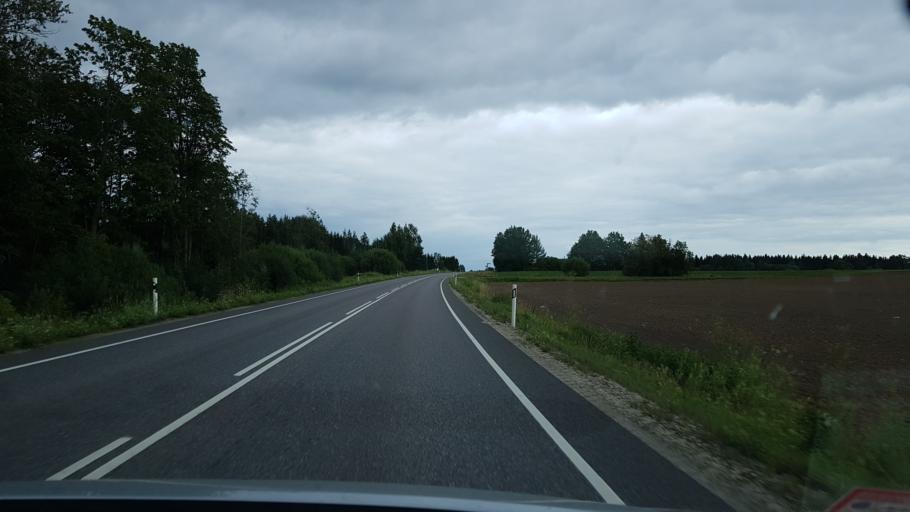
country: EE
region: Tartu
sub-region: Tartu linn
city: Tartu
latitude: 58.4119
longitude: 26.8906
